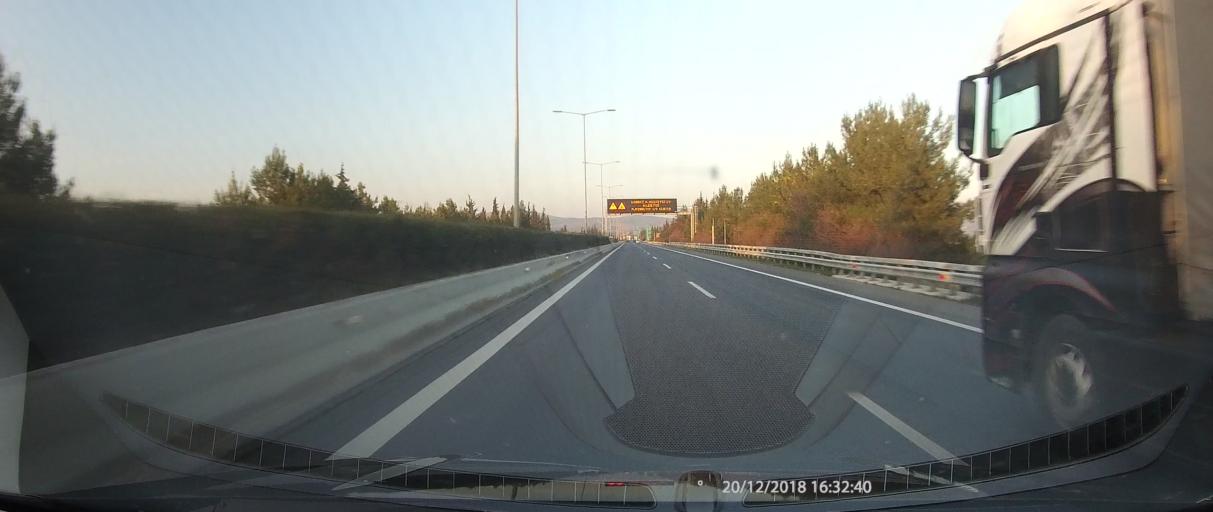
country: GR
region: Thessaly
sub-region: Nomos Magnisias
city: Evxinoupolis
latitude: 39.2491
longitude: 22.7349
